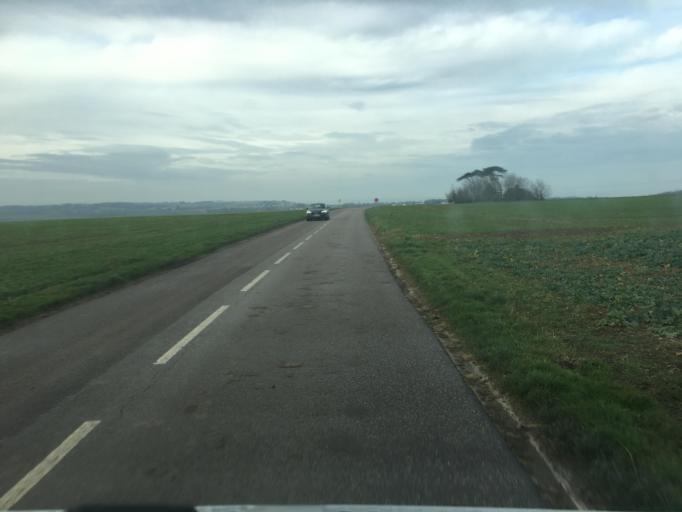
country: FR
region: Lower Normandy
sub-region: Departement du Calvados
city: Ver-sur-Mer
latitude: 49.3214
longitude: -0.5565
